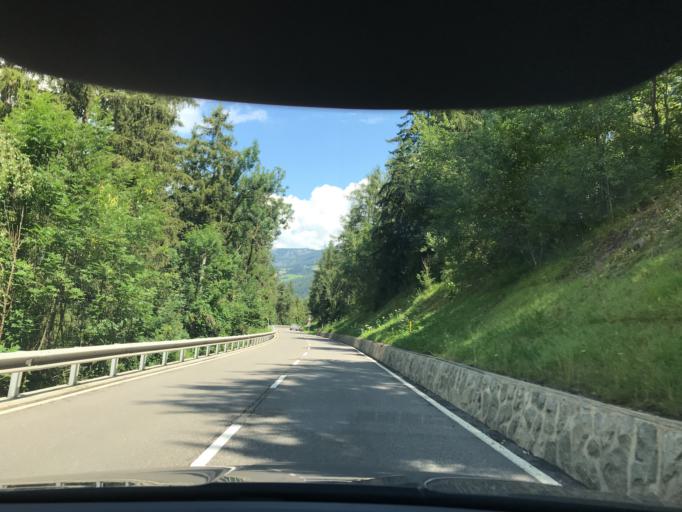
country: IT
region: Trentino-Alto Adige
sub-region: Bolzano
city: Valdaora di Mezzo
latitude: 46.7567
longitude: 12.0215
